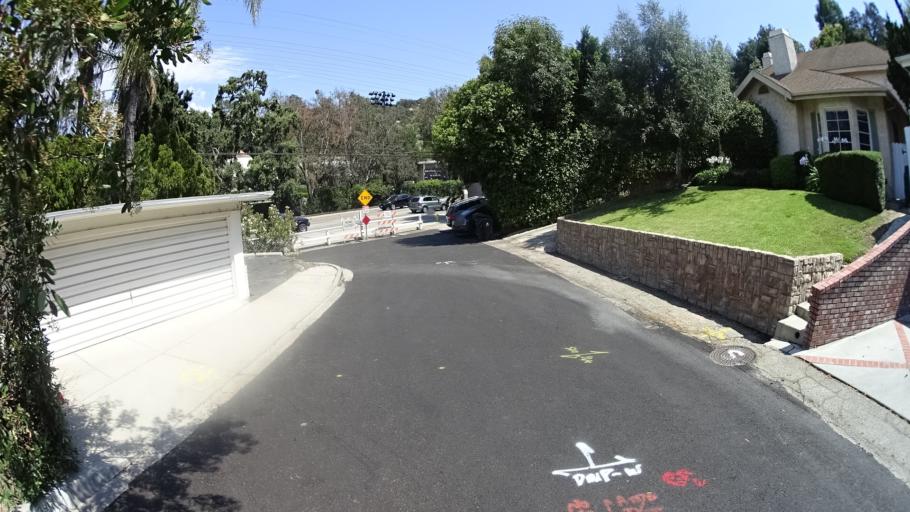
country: US
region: California
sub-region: Los Angeles County
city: Sherman Oaks
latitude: 34.1407
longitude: -118.4140
